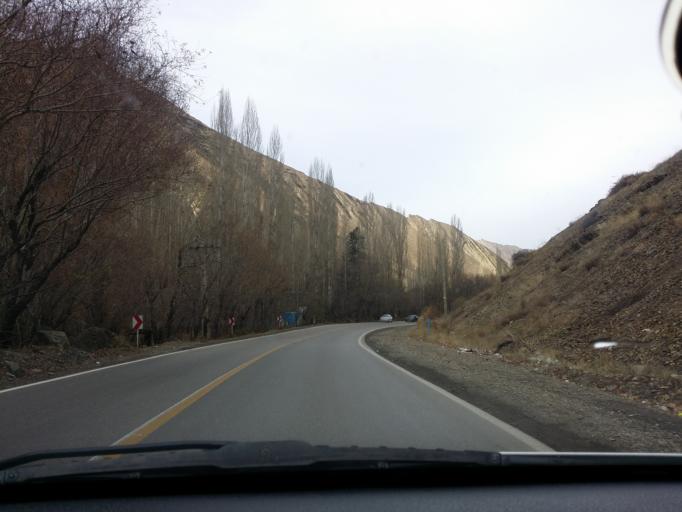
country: IR
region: Tehran
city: Tajrish
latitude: 36.0287
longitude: 51.2269
